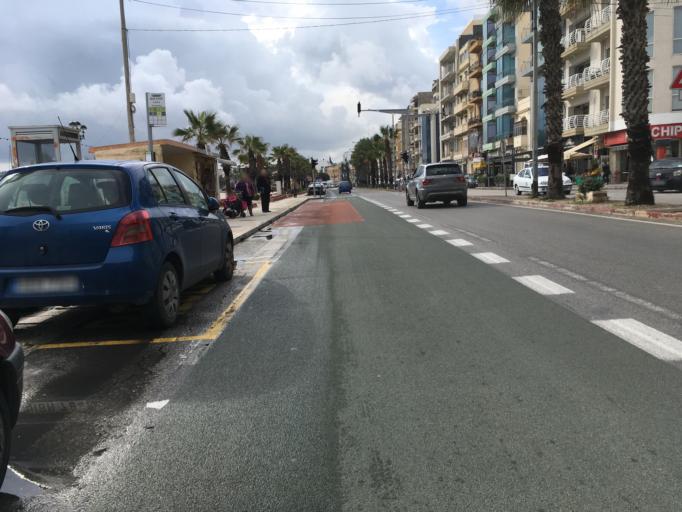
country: MT
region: Tas-Sliema
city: Sliema
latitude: 35.9063
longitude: 14.4976
